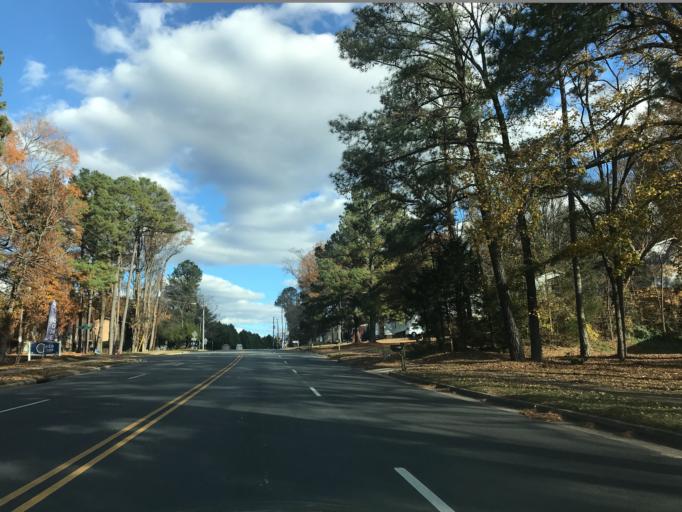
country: US
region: North Carolina
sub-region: Wake County
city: Raleigh
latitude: 35.8353
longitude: -78.5975
